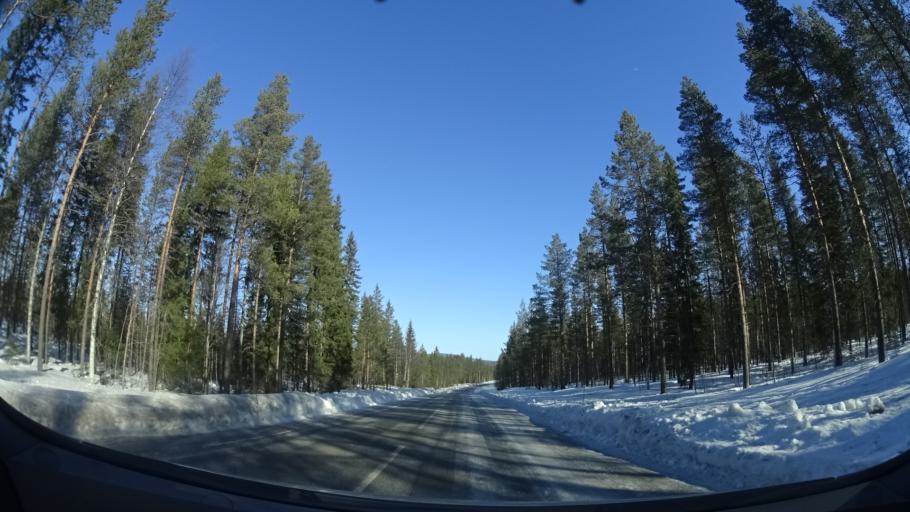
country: SE
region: Vaesterbotten
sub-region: Skelleftea Kommun
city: Langsele
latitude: 65.0906
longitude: 20.0825
